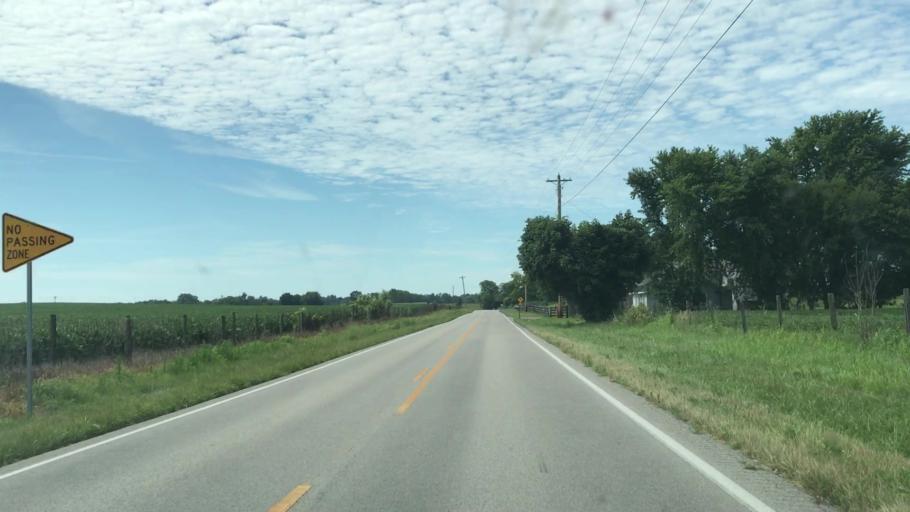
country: US
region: Kentucky
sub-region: Edmonson County
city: Brownsville
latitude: 37.0756
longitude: -86.2159
